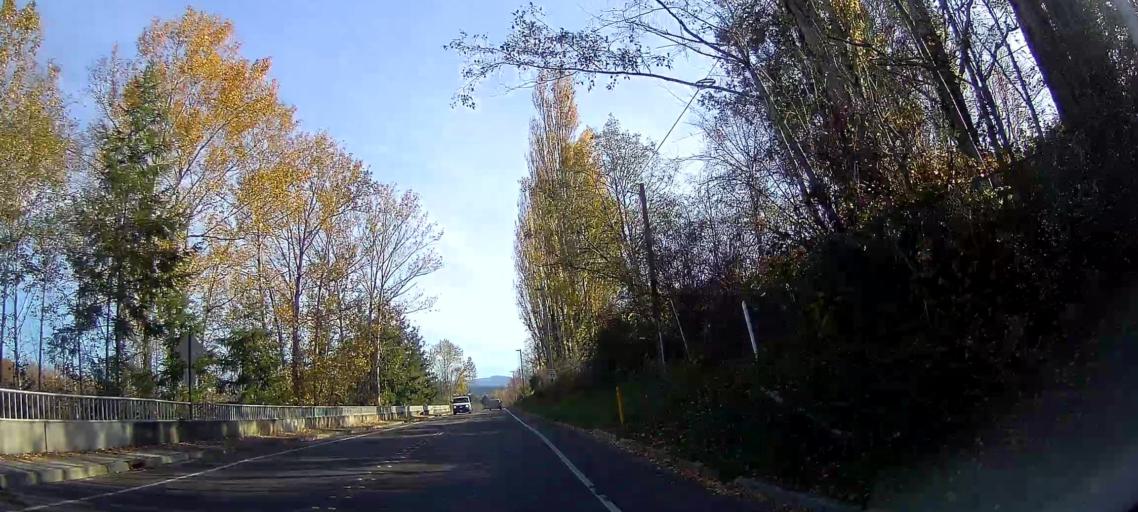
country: US
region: Washington
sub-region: Whatcom County
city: Bellingham
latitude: 48.7751
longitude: -122.4633
